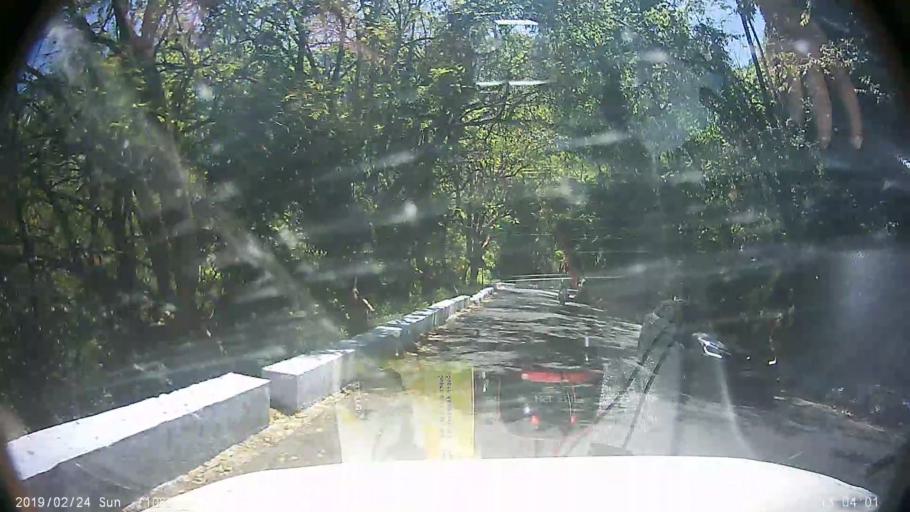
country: IN
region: Tamil Nadu
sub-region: Nilgiri
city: Wellington
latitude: 11.3377
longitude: 76.8283
